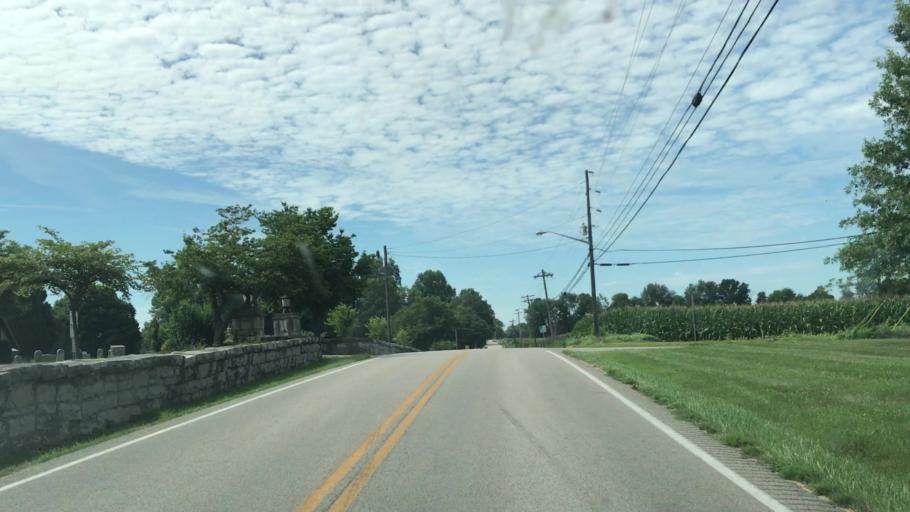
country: US
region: Kentucky
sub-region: Edmonson County
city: Brownsville
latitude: 37.0617
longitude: -86.2114
